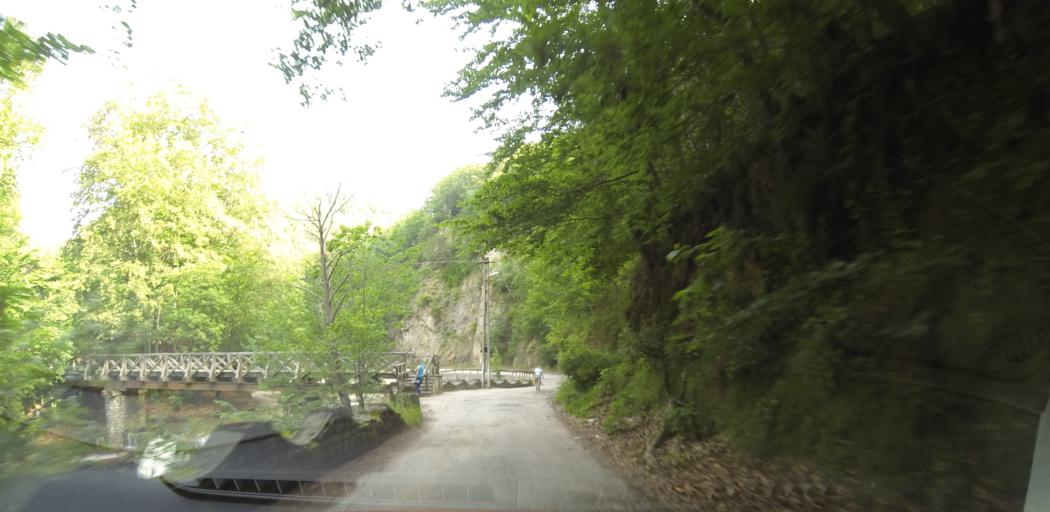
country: RO
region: Valcea
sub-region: Oras Baile Olanesti
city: Livadia
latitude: 45.2087
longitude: 24.2339
